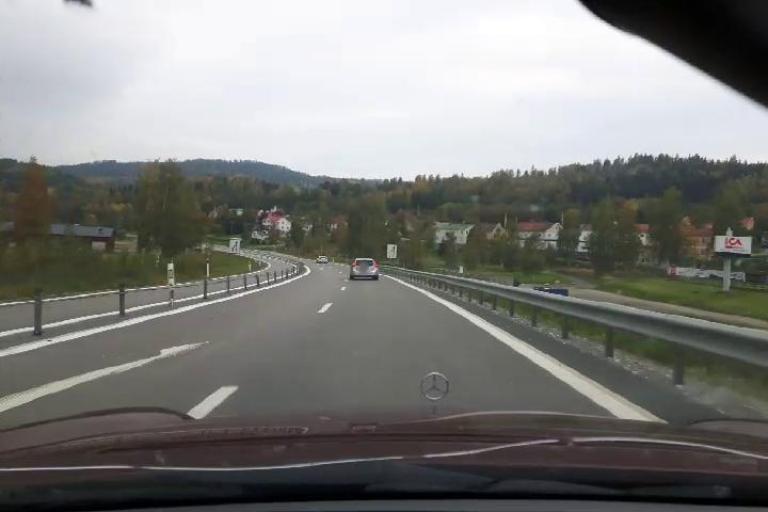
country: SE
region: Vaesternorrland
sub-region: Kramfors Kommun
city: Nordingra
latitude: 63.0512
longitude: 18.3262
